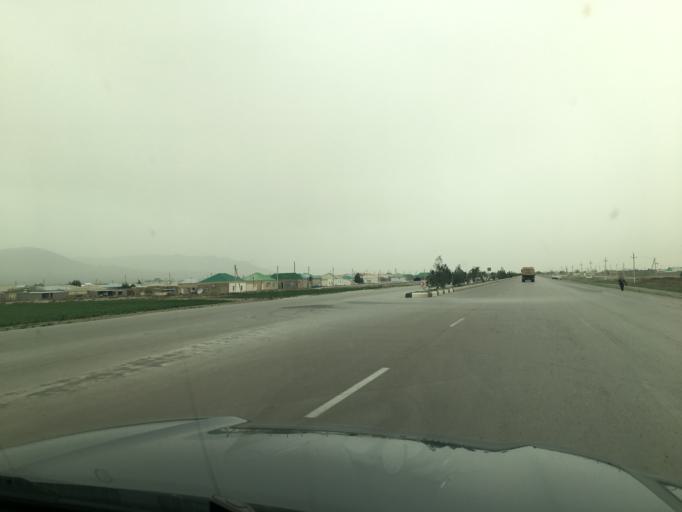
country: TM
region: Ahal
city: Baharly
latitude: 38.3933
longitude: 57.4824
